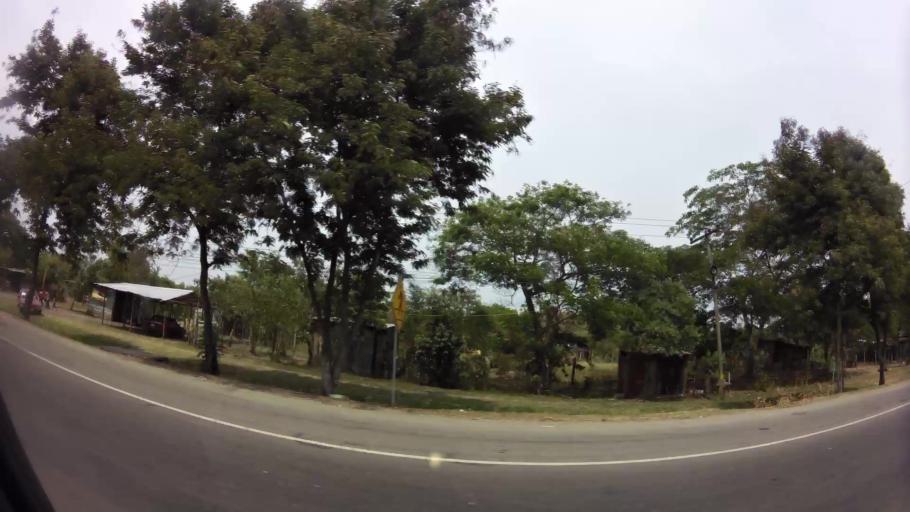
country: HN
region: Cortes
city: Nuevo Chamelecon
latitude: 15.3827
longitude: -87.9899
